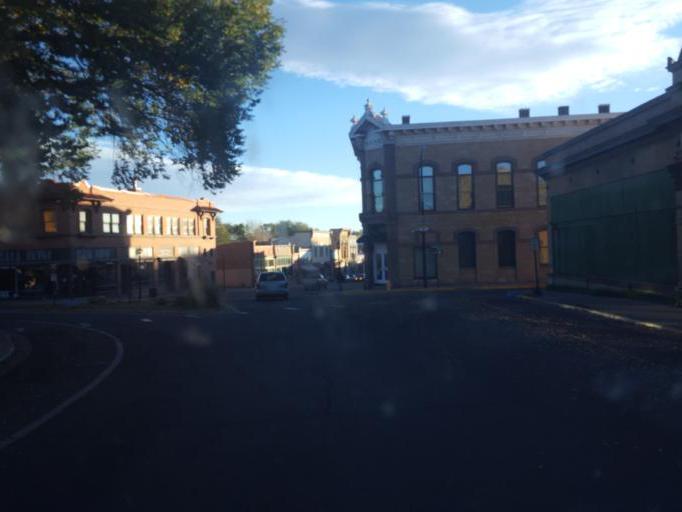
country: US
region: New Mexico
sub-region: San Miguel County
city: Las Vegas
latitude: 35.5926
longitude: -105.2265
